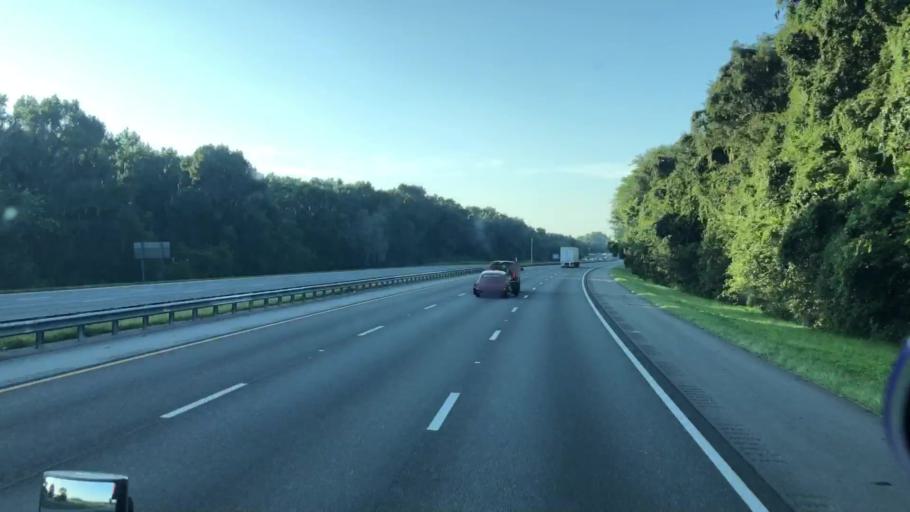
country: US
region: Florida
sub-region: Marion County
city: Citra
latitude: 29.3985
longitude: -82.2416
